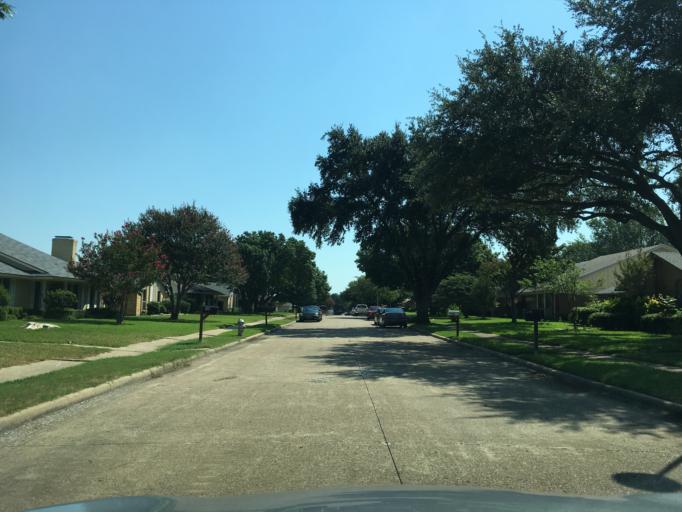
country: US
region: Texas
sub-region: Dallas County
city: Garland
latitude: 32.9357
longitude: -96.6545
